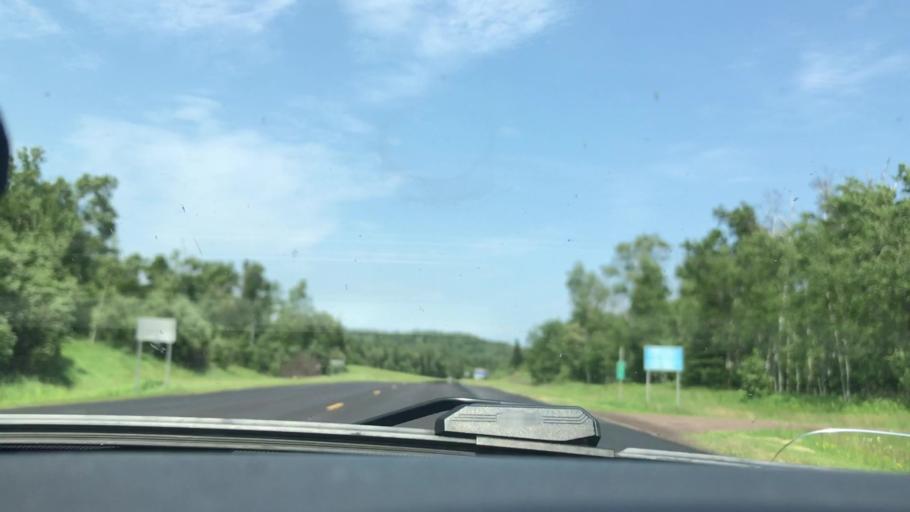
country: US
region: Minnesota
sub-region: Lake County
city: Silver Bay
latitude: 47.3327
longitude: -91.2059
